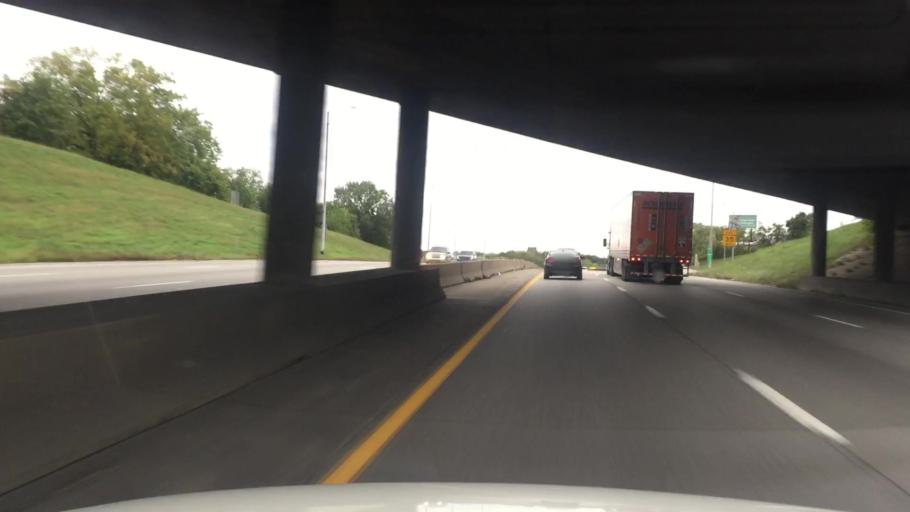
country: US
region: Missouri
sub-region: Jackson County
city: Kansas City
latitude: 39.0789
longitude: -94.5386
